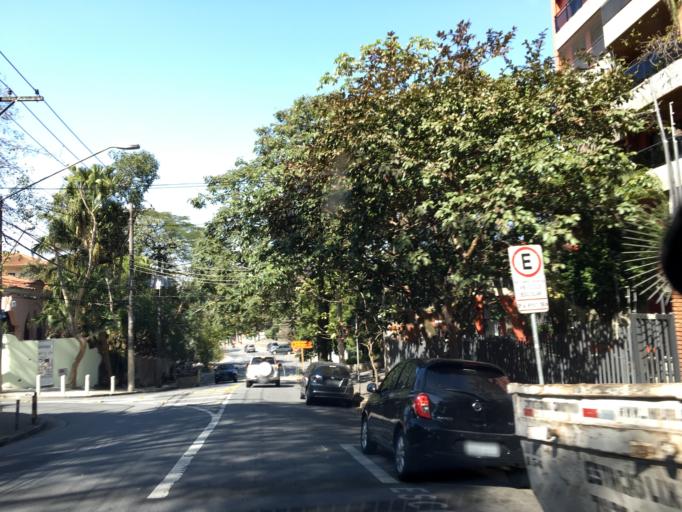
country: BR
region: Sao Paulo
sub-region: Sao Paulo
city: Sao Paulo
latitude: -23.5417
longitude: -46.6698
